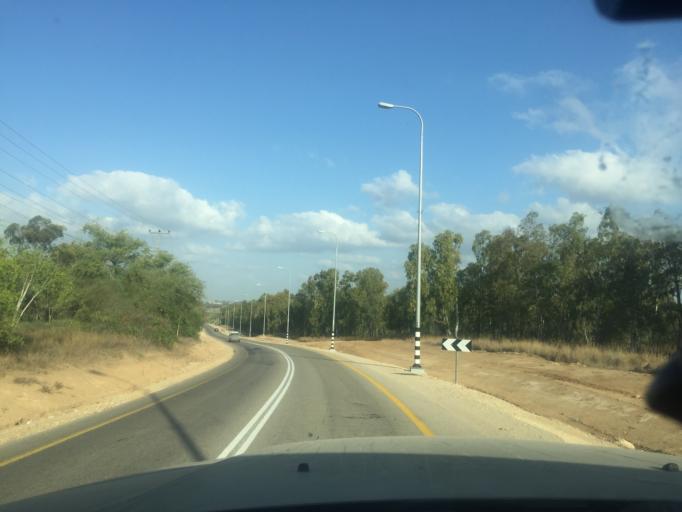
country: PS
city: Umm an Nasr
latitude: 31.6043
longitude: 34.5657
